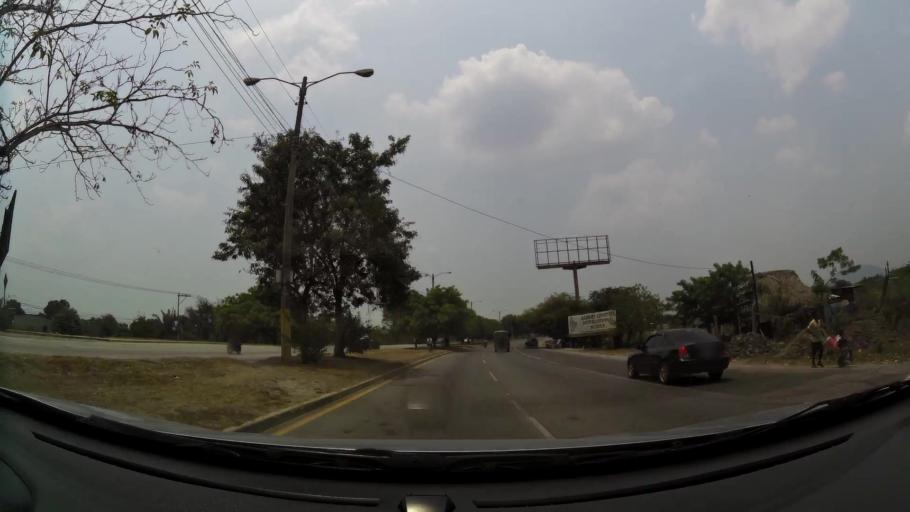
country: HN
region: Cortes
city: La Lima
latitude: 15.4532
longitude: -87.9474
